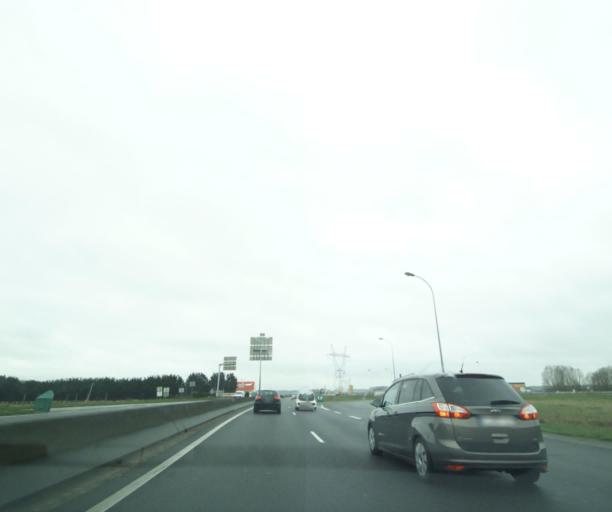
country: FR
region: Ile-de-France
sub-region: Departement de l'Essonne
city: Egly
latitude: 48.5721
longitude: 2.2348
